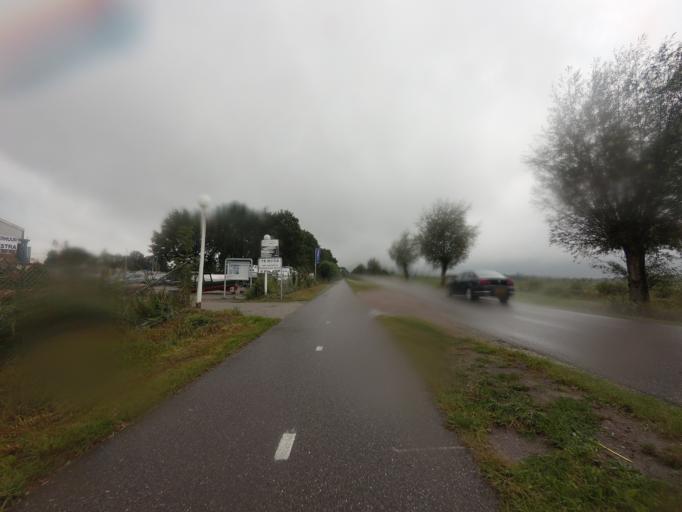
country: NL
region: Friesland
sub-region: Gemeente Tytsjerksteradiel
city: Garyp
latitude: 53.1351
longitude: 5.9463
